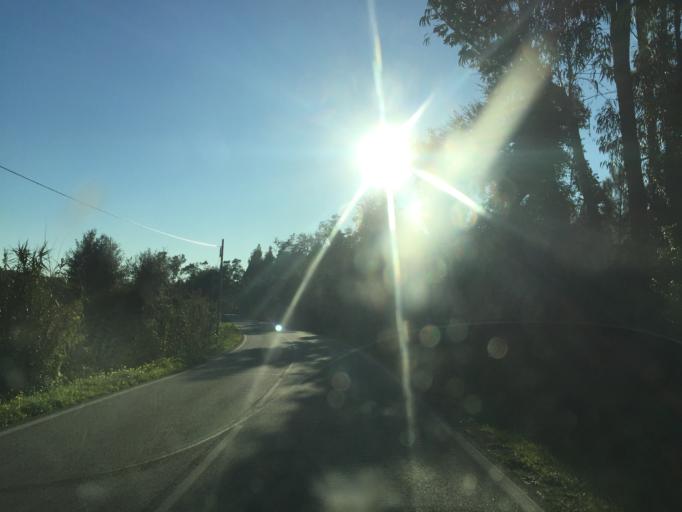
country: PT
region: Coimbra
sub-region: Figueira da Foz
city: Alhadas
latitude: 40.1725
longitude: -8.8039
